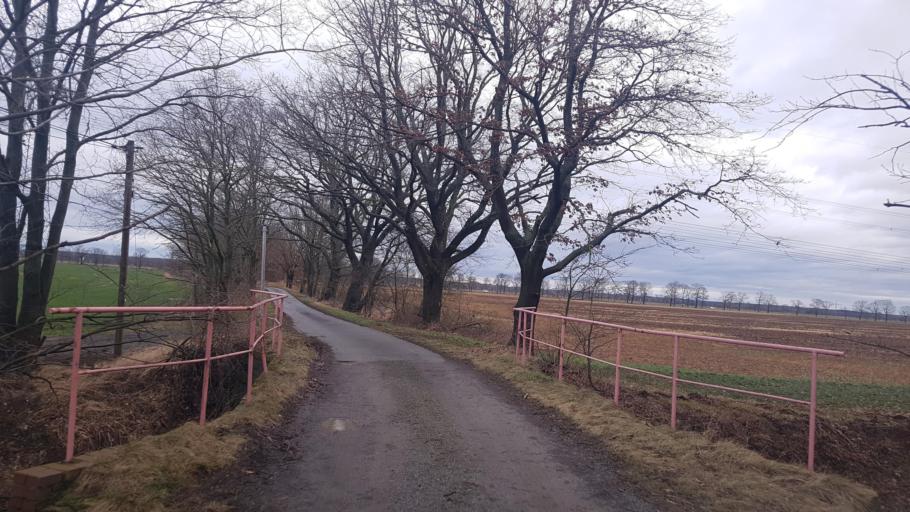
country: DE
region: Brandenburg
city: Plessa
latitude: 51.4477
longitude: 13.6519
